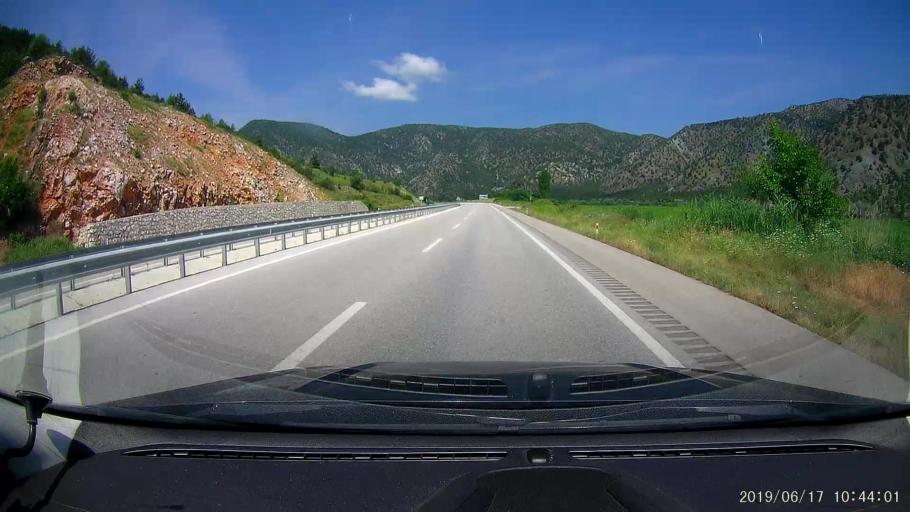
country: TR
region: Corum
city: Kargi
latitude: 41.0709
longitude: 34.5229
